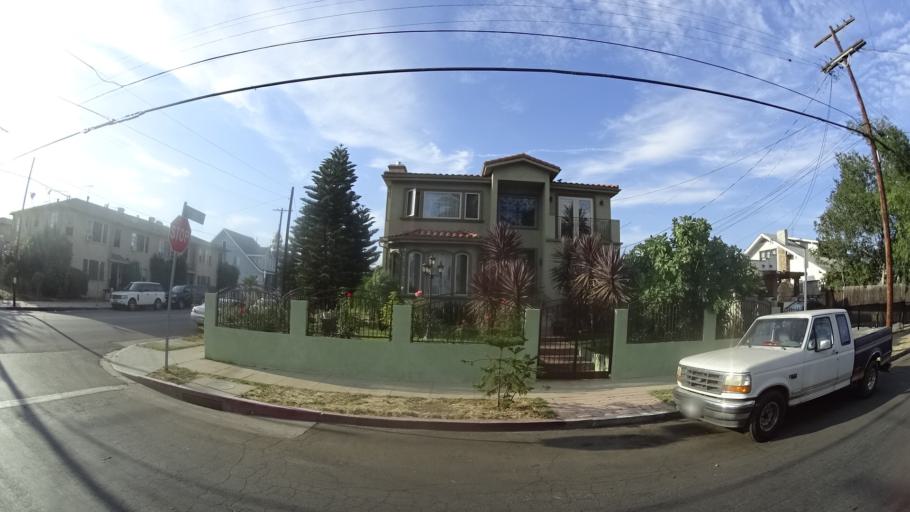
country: US
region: California
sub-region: Los Angeles County
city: Hollywood
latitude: 34.0929
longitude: -118.3067
